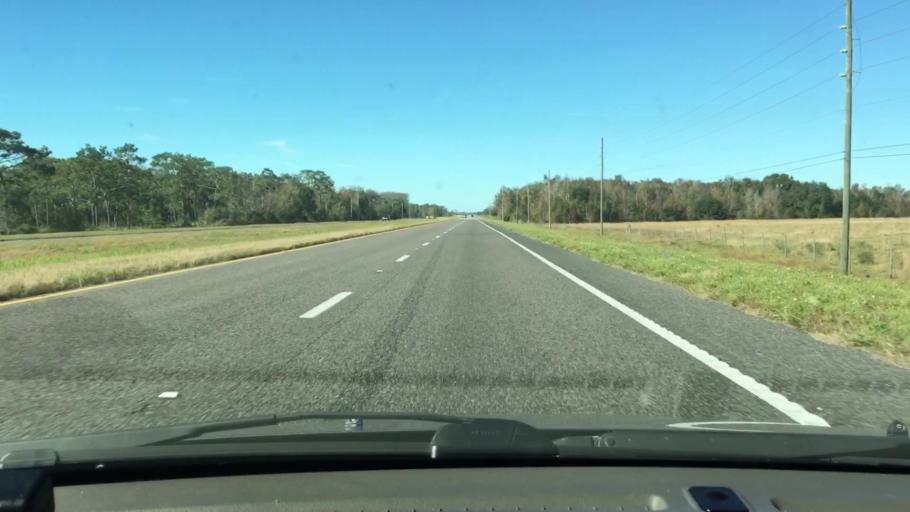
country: US
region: Florida
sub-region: Brevard County
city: June Park
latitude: 28.1227
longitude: -80.9580
